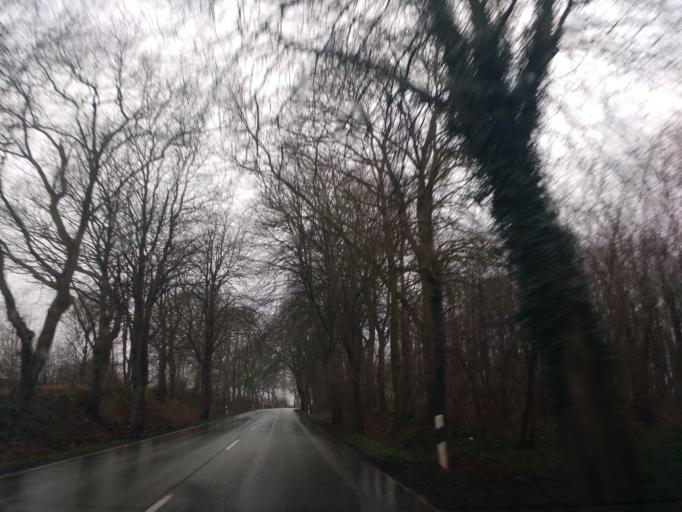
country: DE
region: Schleswig-Holstein
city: Wangels
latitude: 54.2943
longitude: 10.7214
